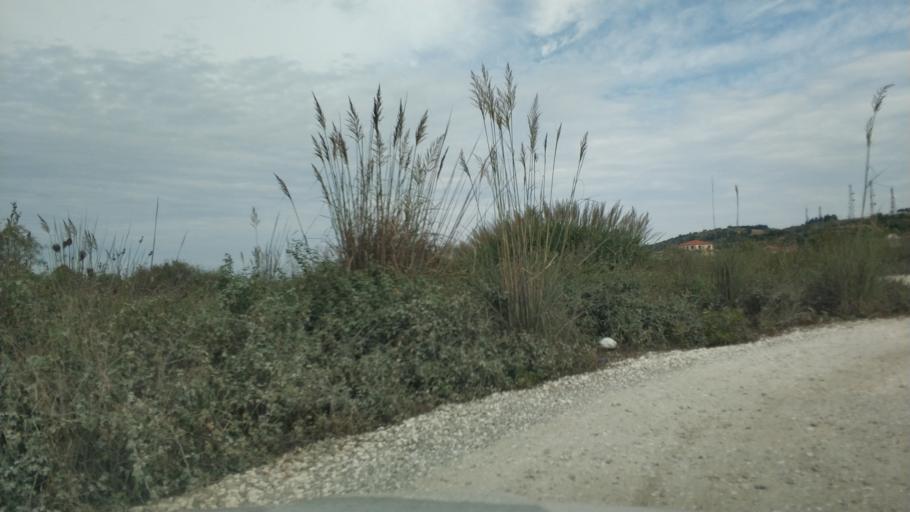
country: AL
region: Vlore
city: Vlore
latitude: 40.5053
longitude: 19.4093
